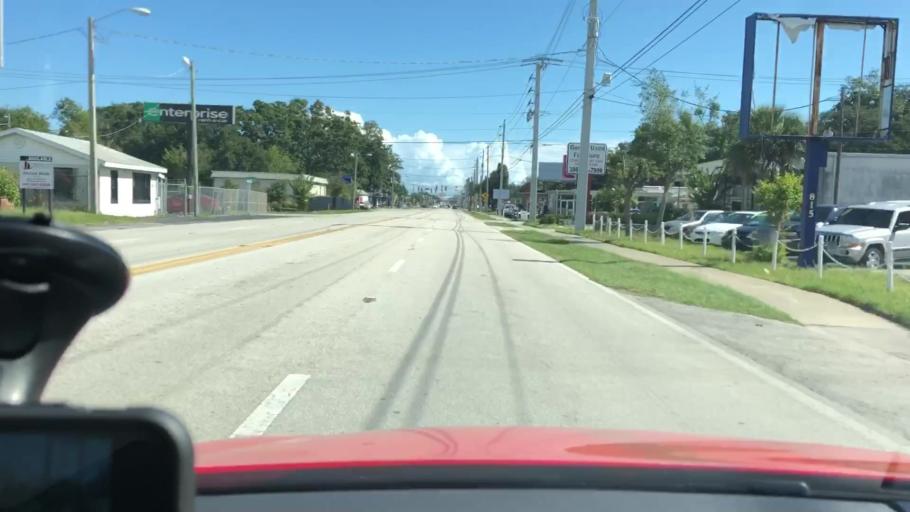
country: US
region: Florida
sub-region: Volusia County
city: Holly Hill
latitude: 29.2220
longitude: -81.0418
